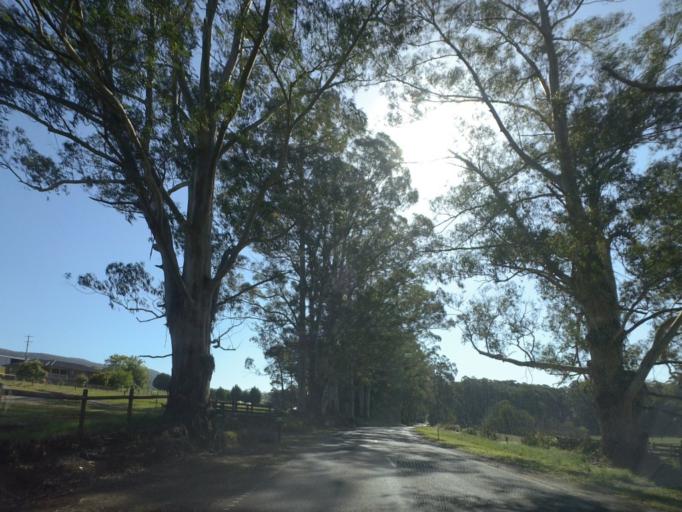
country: AU
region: Victoria
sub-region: Yarra Ranges
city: Millgrove
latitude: -37.8543
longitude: 145.7065
